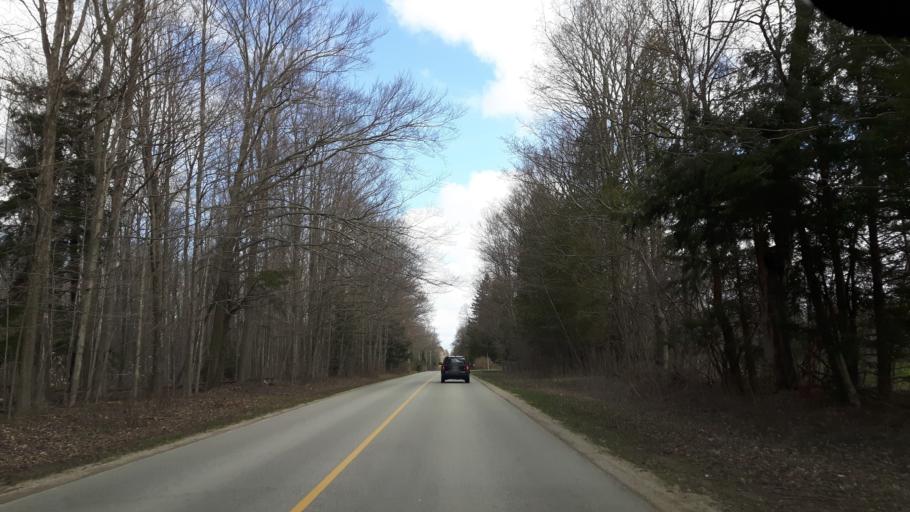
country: CA
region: Ontario
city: Bluewater
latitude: 43.5943
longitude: -81.6848
